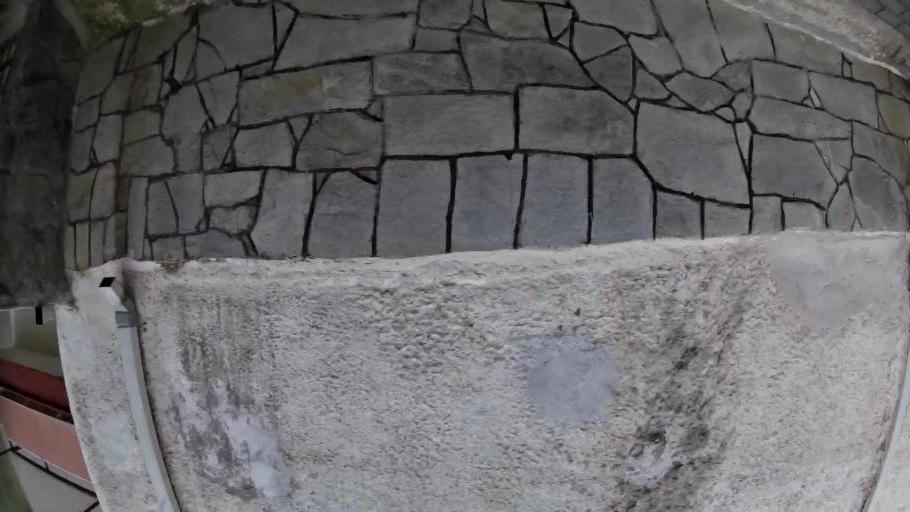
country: GR
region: Central Macedonia
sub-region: Nomos Thessalonikis
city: Stavroupoli
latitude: 40.6685
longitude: 22.9396
